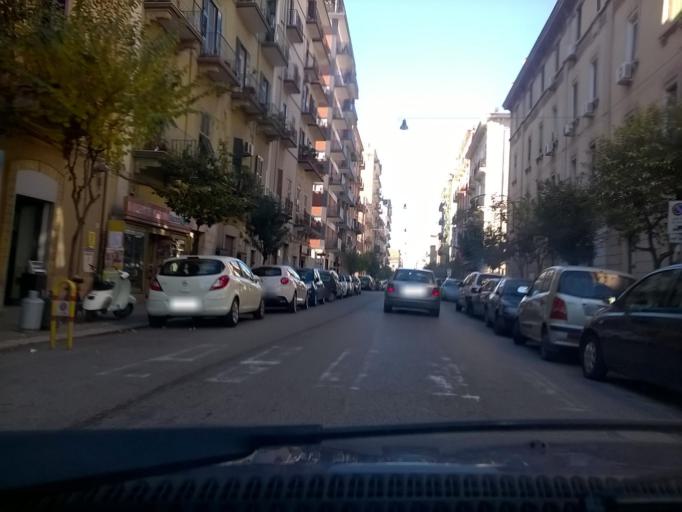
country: IT
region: Apulia
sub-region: Provincia di Taranto
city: Taranto
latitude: 40.4650
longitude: 17.2528
